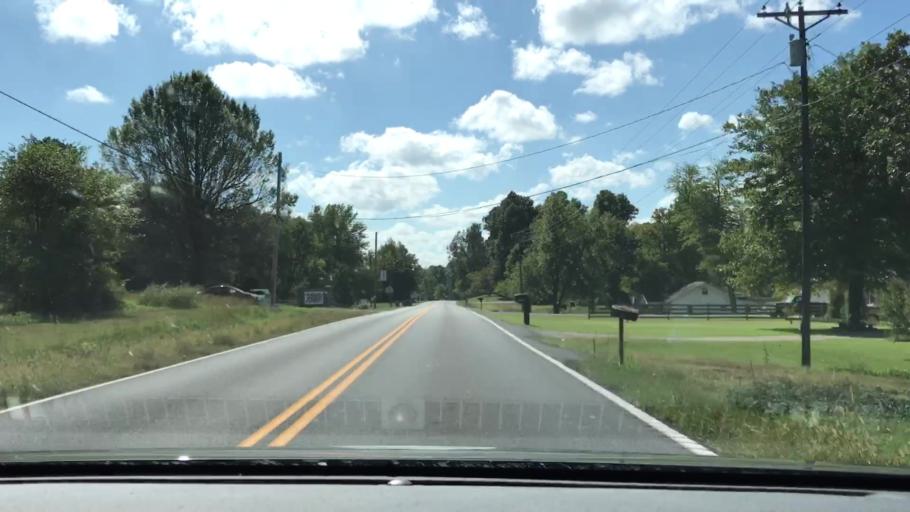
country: US
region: Kentucky
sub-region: McCracken County
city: Reidland
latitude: 36.9152
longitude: -88.5208
